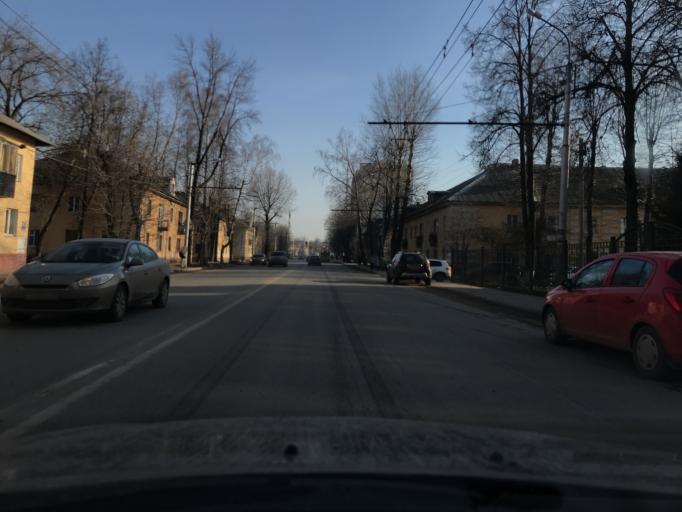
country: RU
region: Kaluga
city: Kaluga
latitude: 54.5303
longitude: 36.2613
